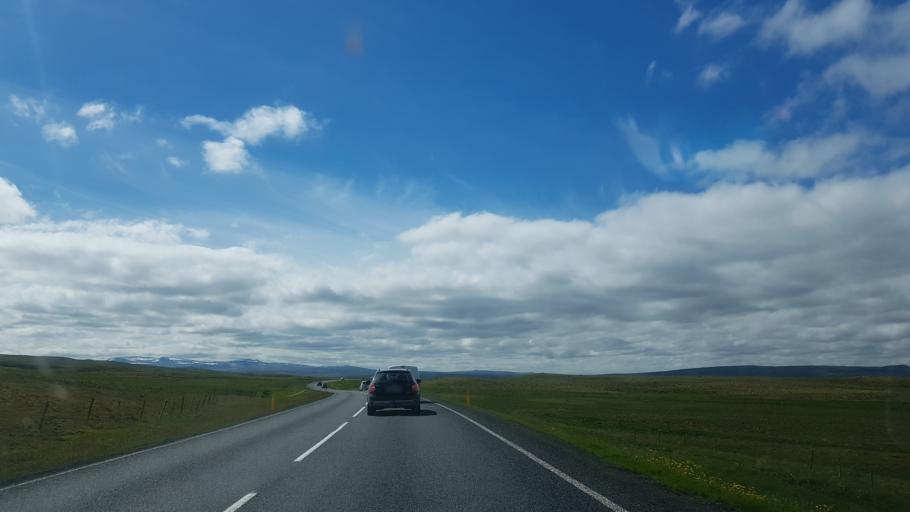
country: IS
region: West
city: Borgarnes
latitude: 65.2862
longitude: -21.0425
